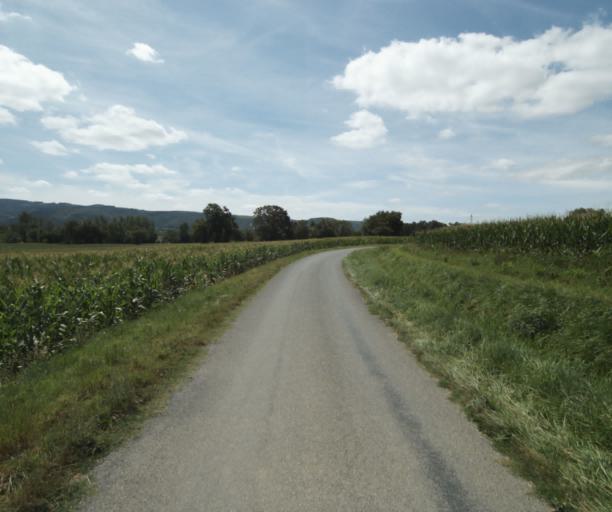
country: FR
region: Midi-Pyrenees
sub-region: Departement du Tarn
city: Soreze
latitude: 43.4837
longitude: 2.0779
